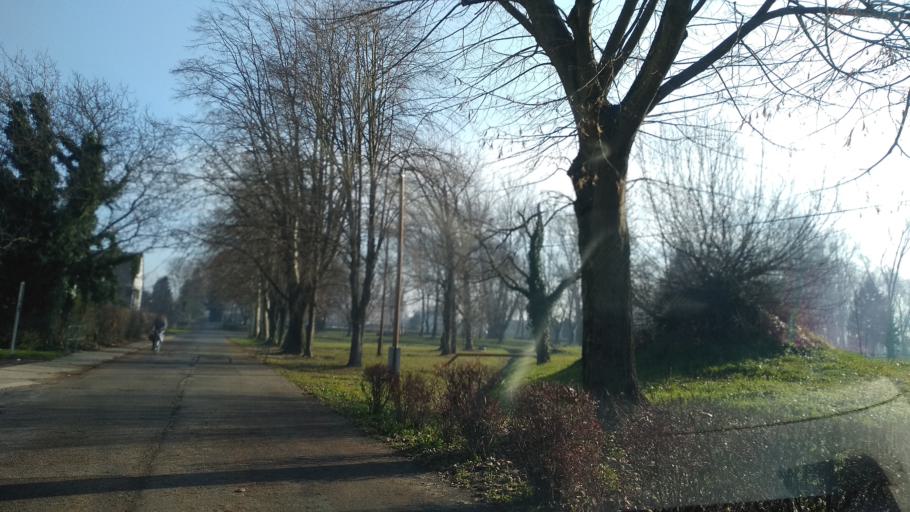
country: HU
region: Somogy
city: Barcs
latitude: 45.9563
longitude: 17.4612
